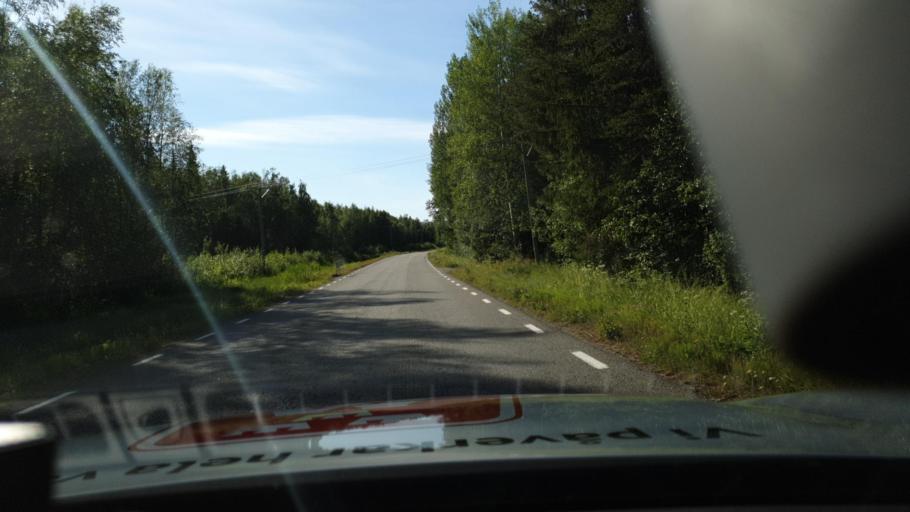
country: SE
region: Norrbotten
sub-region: Kalix Kommun
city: Toere
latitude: 65.8902
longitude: 22.6471
